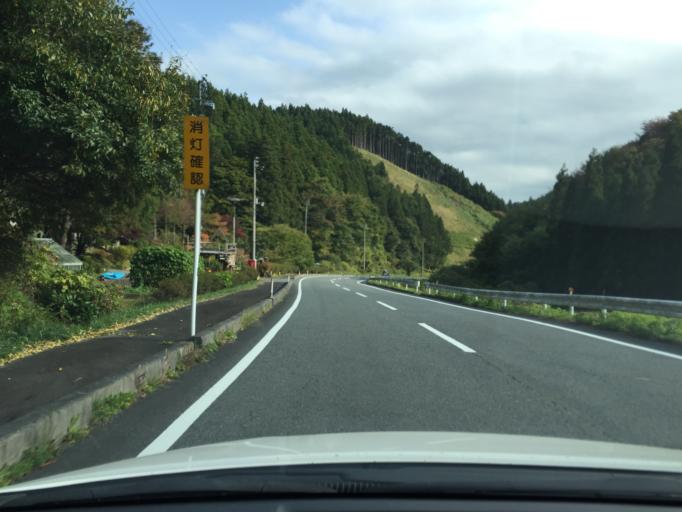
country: JP
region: Ibaraki
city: Kitaibaraki
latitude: 36.9562
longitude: 140.6241
